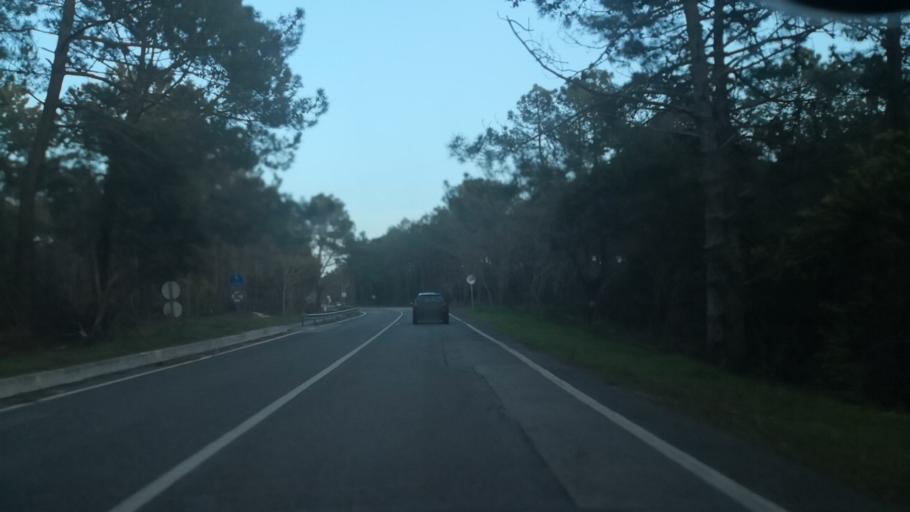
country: PT
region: Leiria
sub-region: Alcobaca
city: Pataias
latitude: 39.7521
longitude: -9.0203
